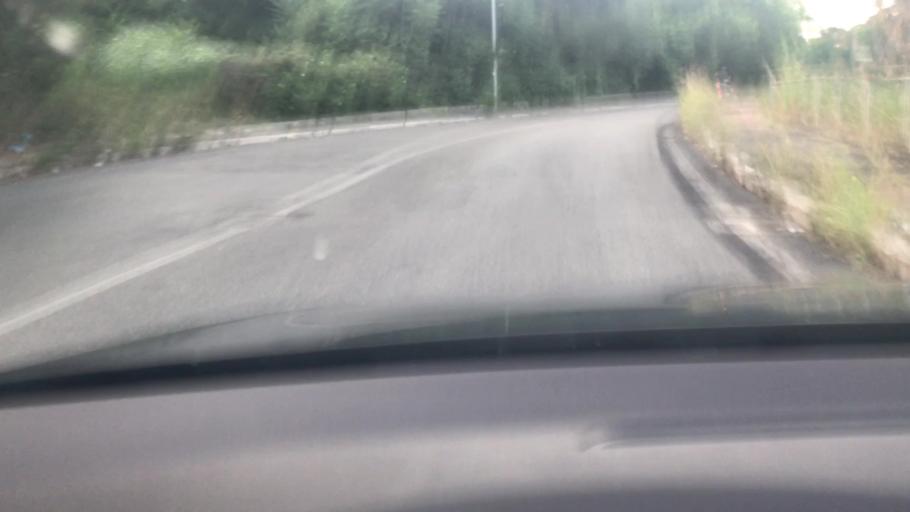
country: IT
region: Latium
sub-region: Citta metropolitana di Roma Capitale
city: Rome
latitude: 41.9267
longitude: 12.5635
